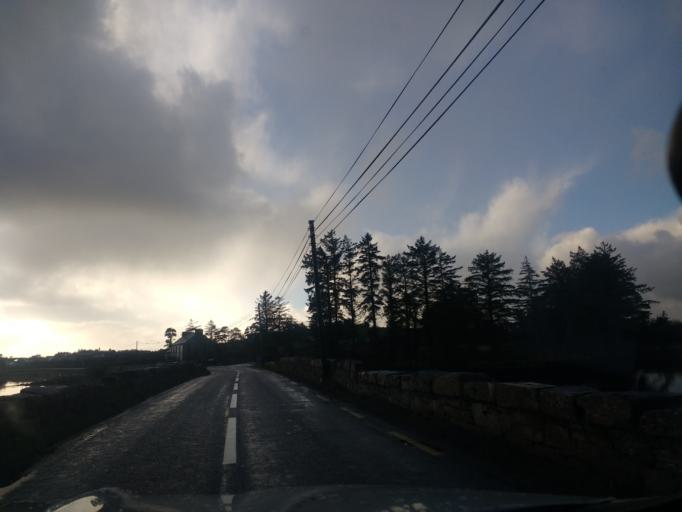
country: IE
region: Ulster
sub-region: County Donegal
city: Ramelton
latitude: 55.0745
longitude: -7.5965
